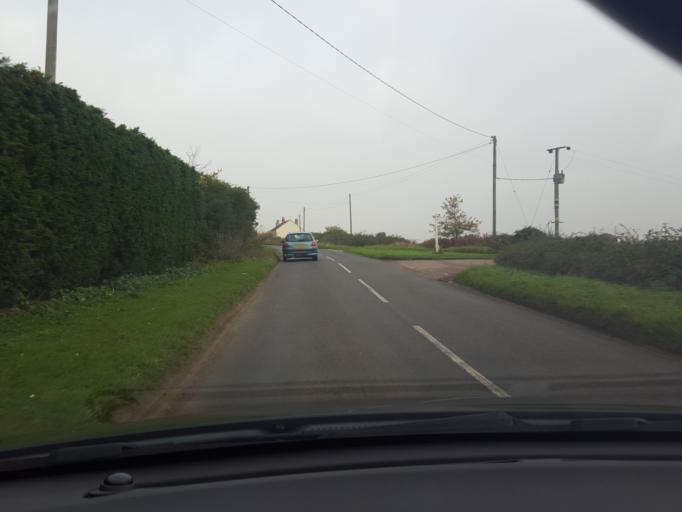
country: GB
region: England
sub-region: Essex
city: Saint Osyth
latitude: 51.7856
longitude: 1.0865
